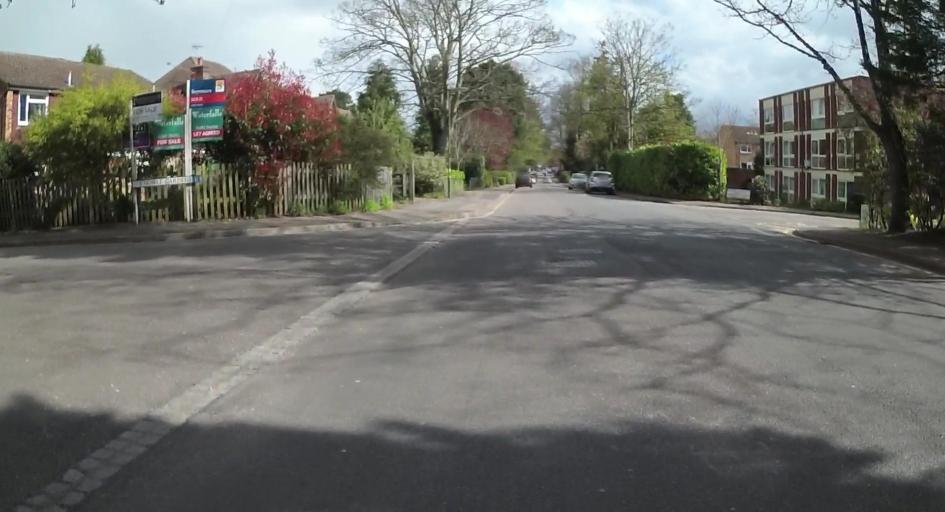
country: GB
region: England
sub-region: Surrey
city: West Byfleet
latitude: 51.3371
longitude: -0.5090
